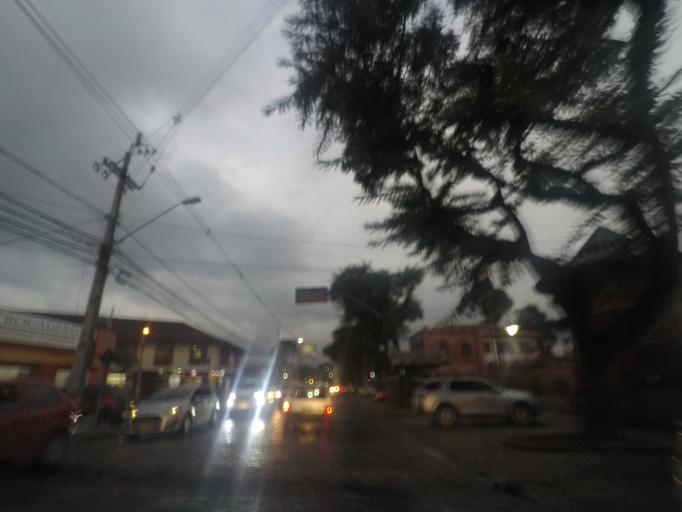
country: BR
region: Parana
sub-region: Curitiba
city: Curitiba
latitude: -25.4030
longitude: -49.3303
